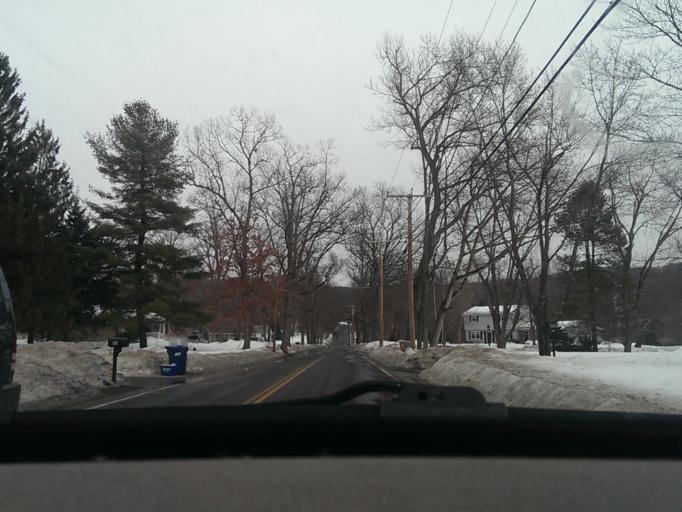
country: US
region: Massachusetts
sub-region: Hampden County
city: Wilbraham
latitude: 42.0930
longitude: -72.4408
